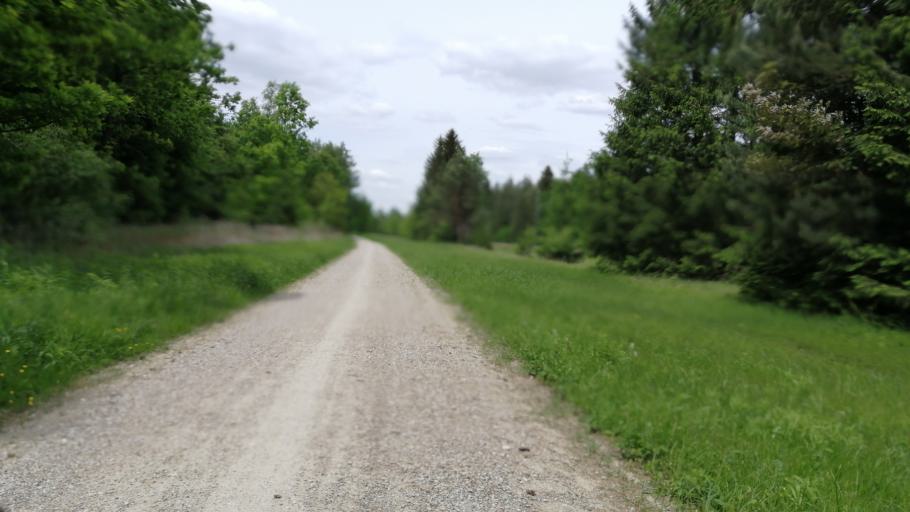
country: DE
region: Bavaria
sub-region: Upper Bavaria
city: Pullach im Isartal
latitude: 48.0668
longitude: 11.5608
